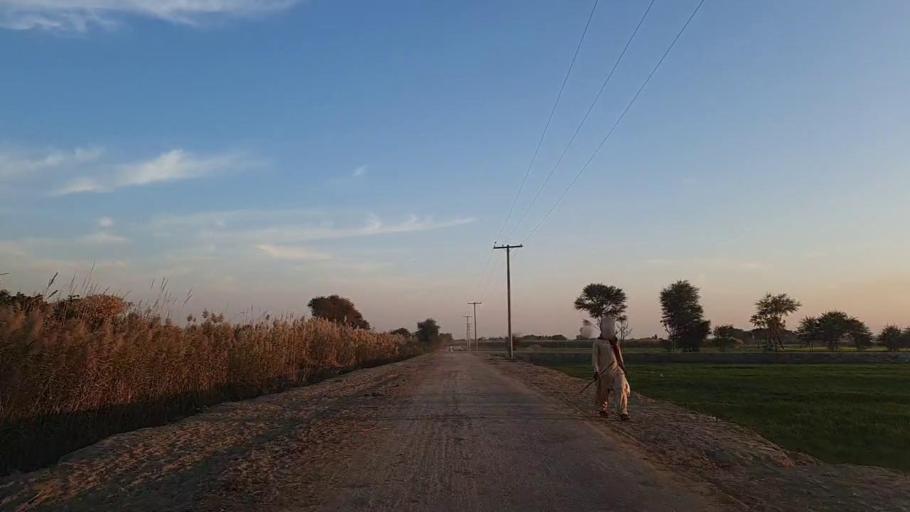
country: PK
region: Sindh
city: Bandhi
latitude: 26.6232
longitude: 68.3726
